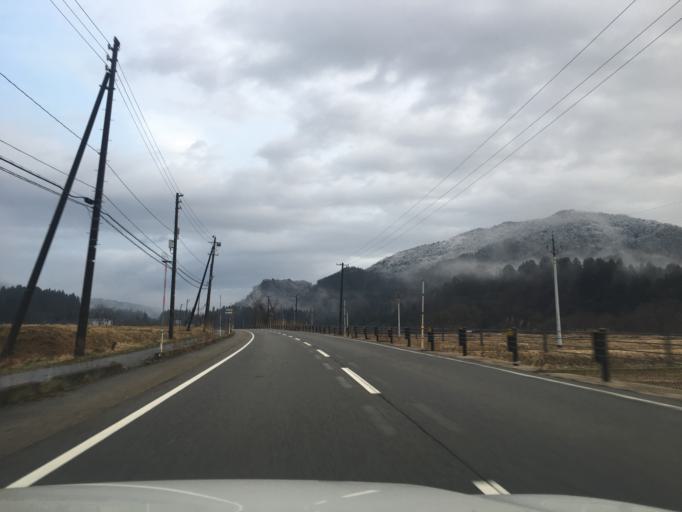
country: JP
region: Niigata
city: Murakami
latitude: 38.3567
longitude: 139.5519
